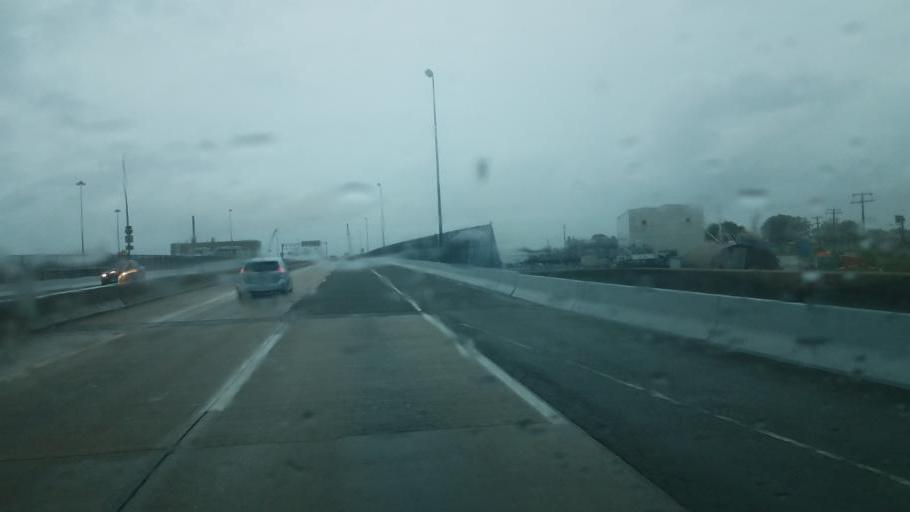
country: US
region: Virginia
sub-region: City of Newport News
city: Newport News
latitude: 36.9623
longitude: -76.4120
